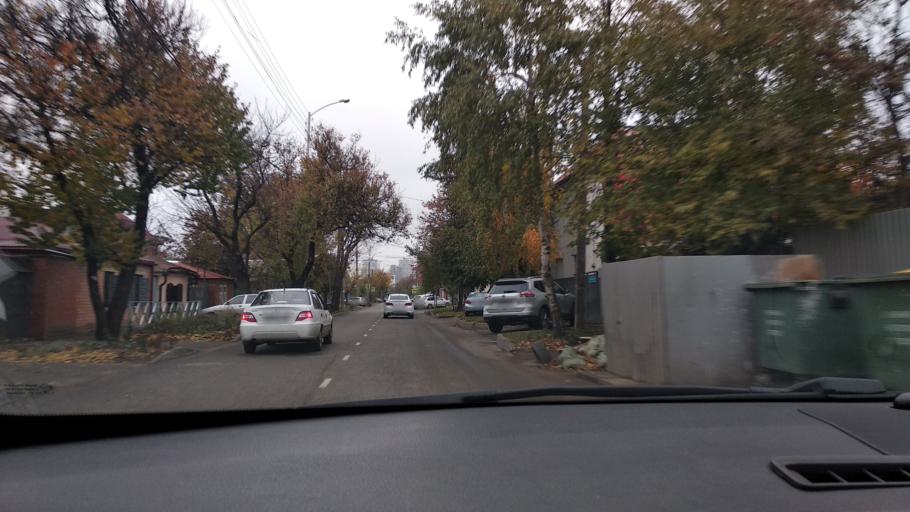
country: RU
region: Krasnodarskiy
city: Krasnodar
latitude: 45.0305
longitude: 38.9885
